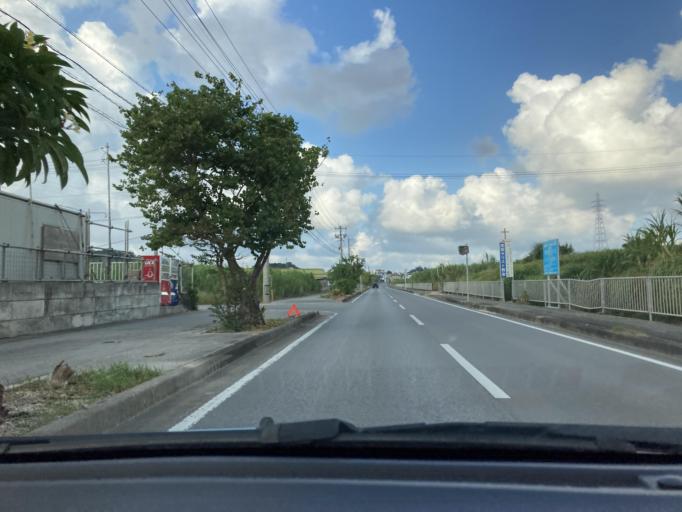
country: JP
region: Okinawa
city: Itoman
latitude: 26.1452
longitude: 127.7042
